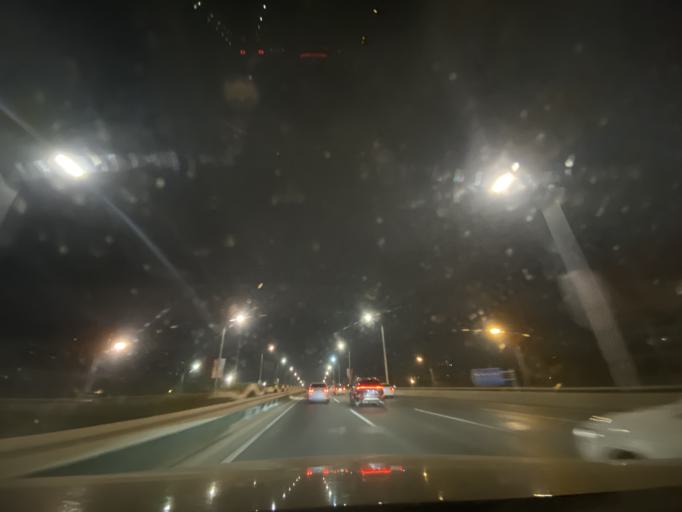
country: CN
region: Beijing
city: Lugu
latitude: 39.8958
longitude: 116.2254
